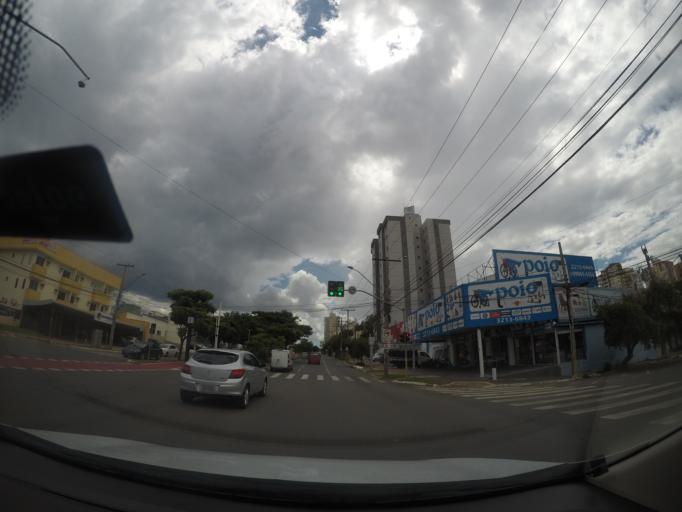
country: BR
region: Goias
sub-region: Goiania
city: Goiania
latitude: -16.6787
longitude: -49.2500
